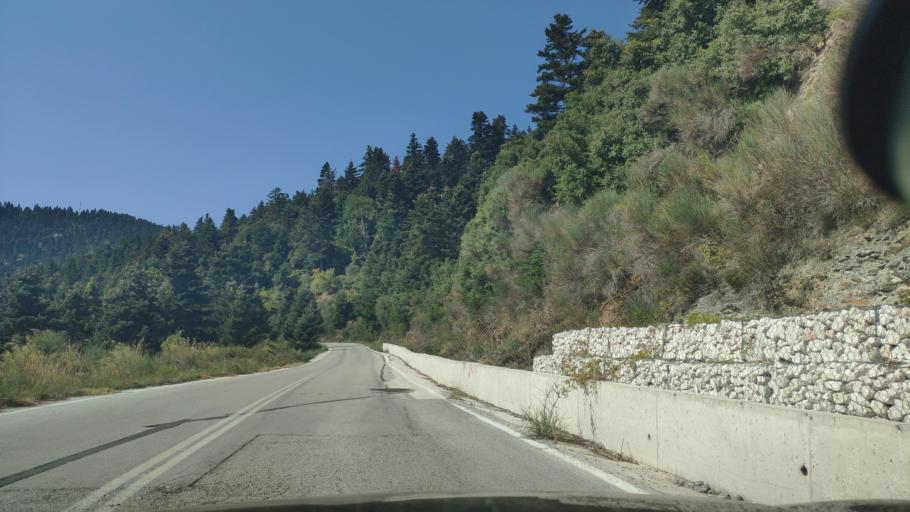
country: GR
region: West Greece
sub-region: Nomos Achaias
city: Aiyira
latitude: 37.8671
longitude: 22.3758
